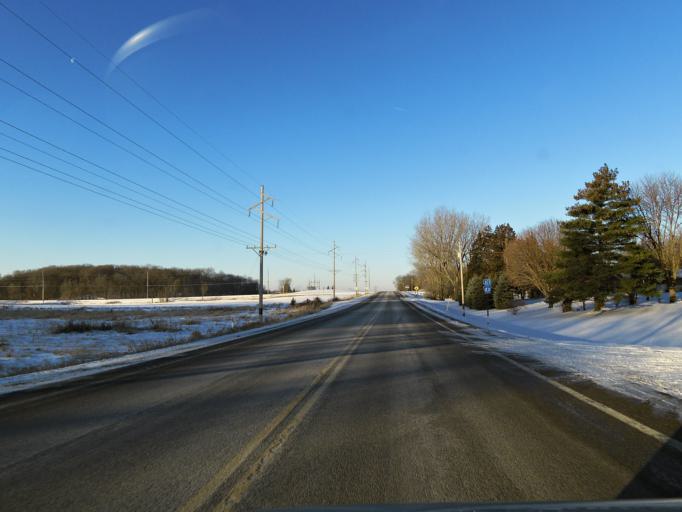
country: US
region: Minnesota
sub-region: Scott County
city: Prior Lake
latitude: 44.6742
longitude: -93.4364
